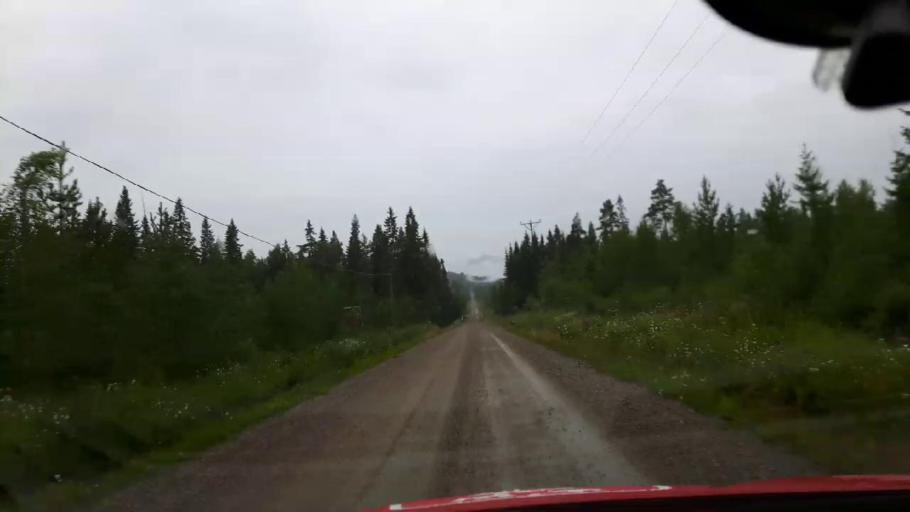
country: SE
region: Jaemtland
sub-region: OEstersunds Kommun
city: Brunflo
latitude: 62.7765
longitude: 14.9863
